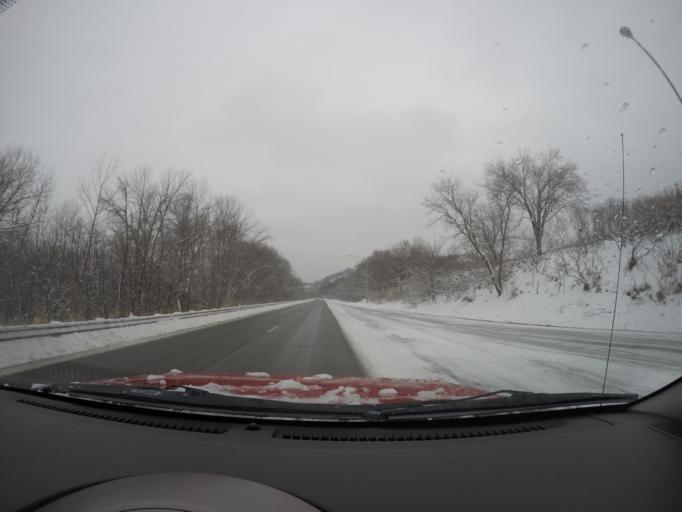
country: US
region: Wisconsin
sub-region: La Crosse County
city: Brice Prairie
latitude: 43.9195
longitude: -91.3708
